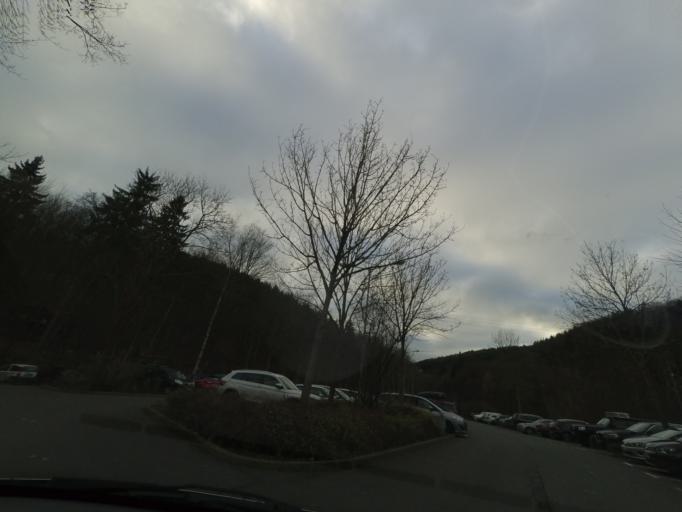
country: DE
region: Thuringia
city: Saalfeld
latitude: 50.6353
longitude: 11.3411
